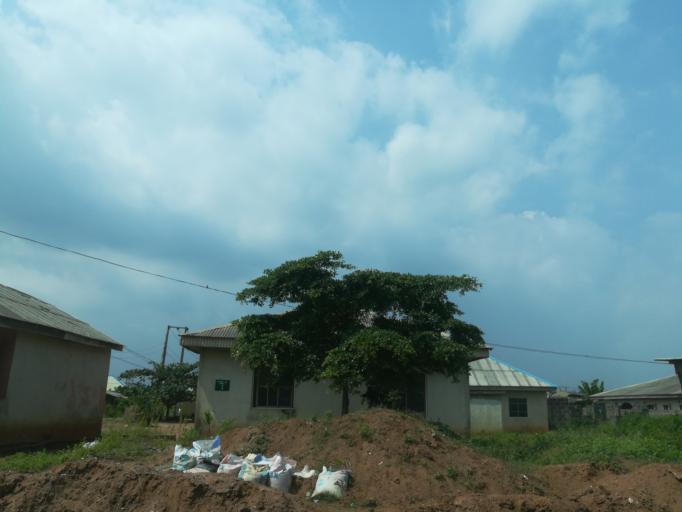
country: NG
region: Lagos
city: Ikorodu
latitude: 6.5996
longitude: 3.6277
